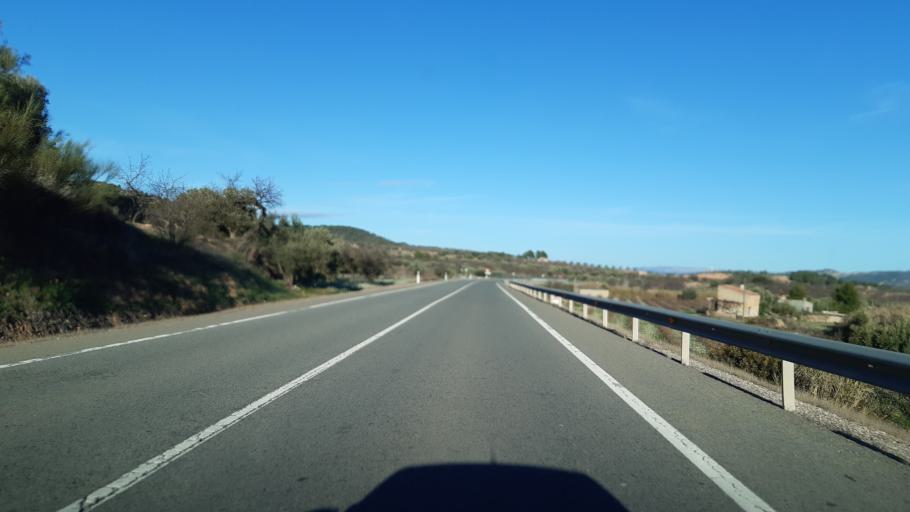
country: ES
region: Catalonia
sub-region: Provincia de Tarragona
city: Gandesa
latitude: 41.0821
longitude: 0.4882
